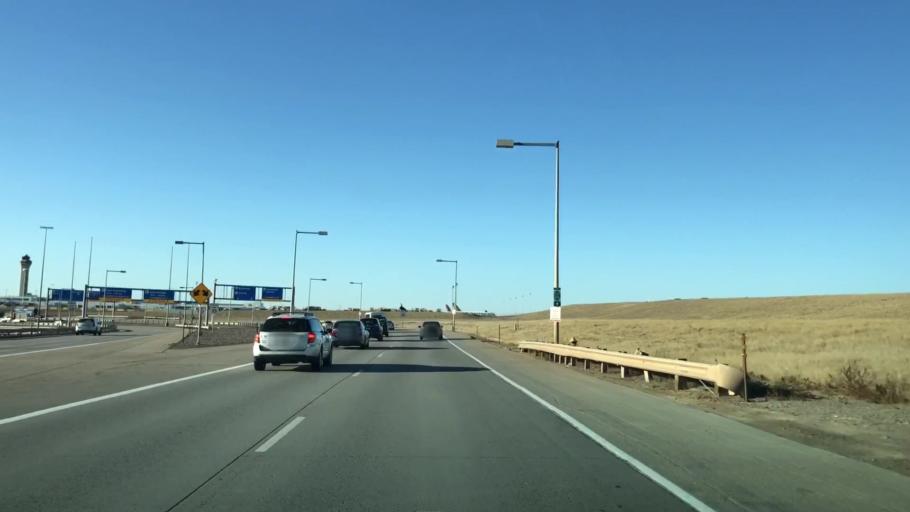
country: US
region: Colorado
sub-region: Weld County
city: Lochbuie
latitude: 39.8483
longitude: -104.6655
